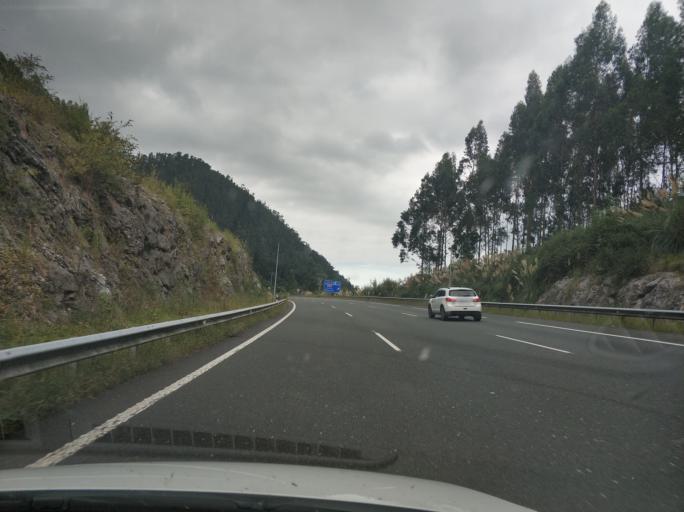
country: ES
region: Cantabria
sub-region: Provincia de Cantabria
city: Cartes
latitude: 43.2954
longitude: -4.0772
